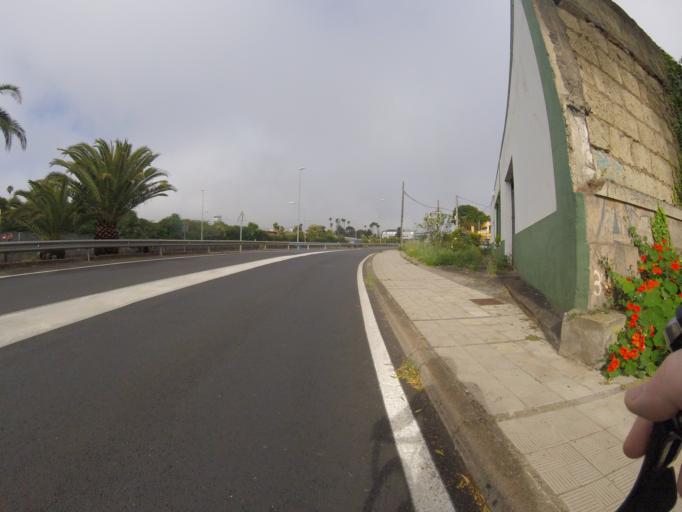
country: ES
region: Canary Islands
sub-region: Provincia de Santa Cruz de Tenerife
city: La Laguna
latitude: 28.4899
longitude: -16.3386
